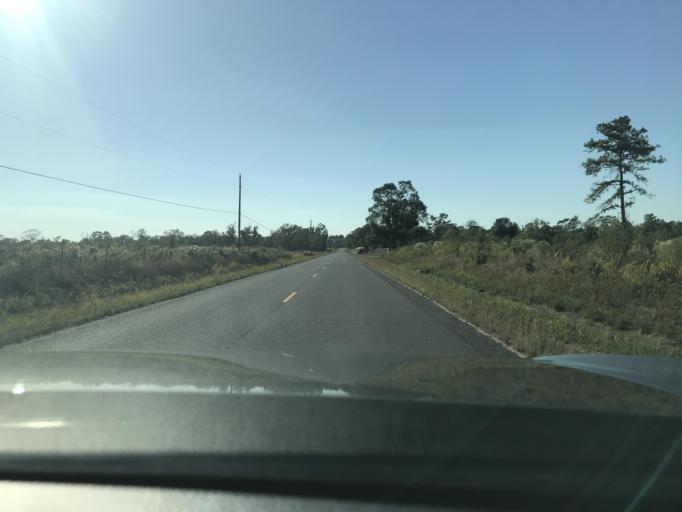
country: US
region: Louisiana
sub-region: Calcasieu Parish
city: Moss Bluff
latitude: 30.3153
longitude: -93.2614
